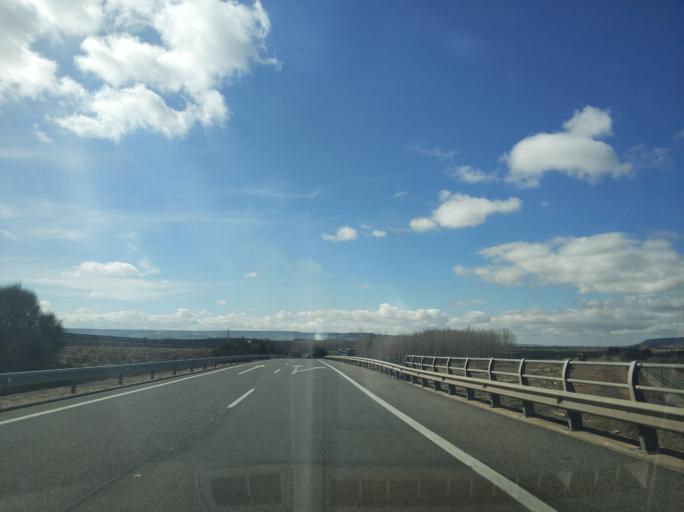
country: ES
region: Castille and Leon
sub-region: Provincia de Burgos
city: Villaverde-Mogina
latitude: 42.1645
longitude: -4.0747
